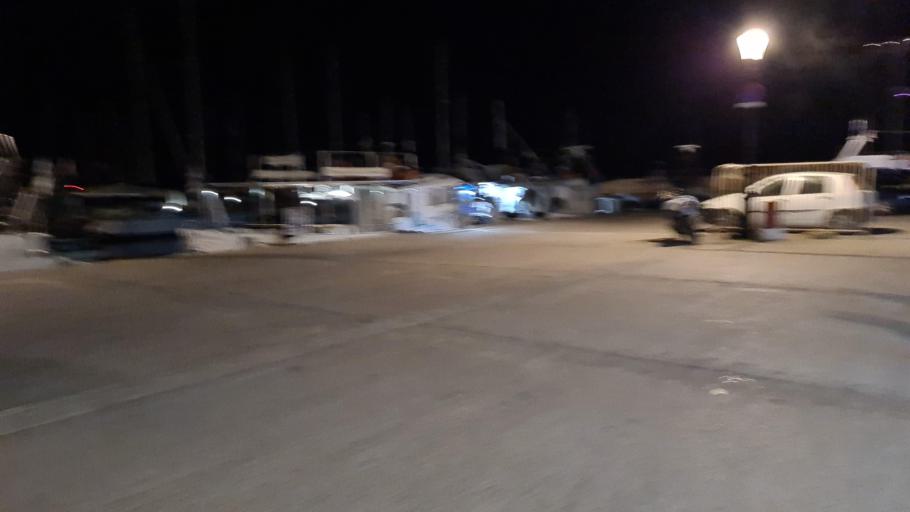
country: GR
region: Crete
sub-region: Nomos Chanias
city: Chania
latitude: 35.5184
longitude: 24.0214
